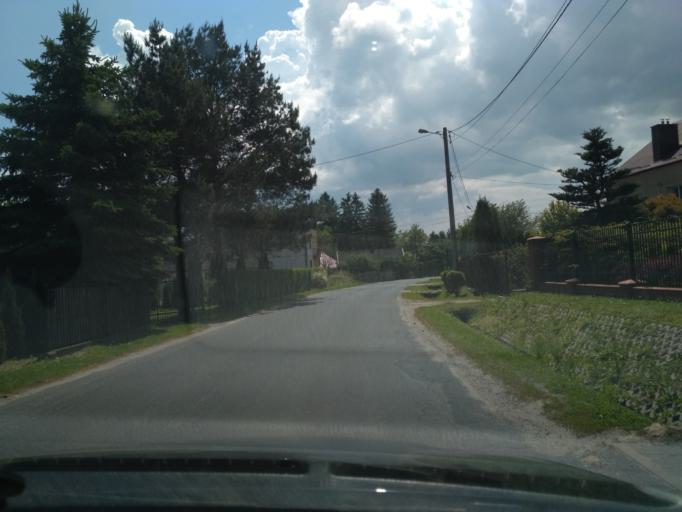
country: PL
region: Subcarpathian Voivodeship
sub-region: Powiat lancucki
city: Sonina
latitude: 50.0588
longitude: 22.2682
